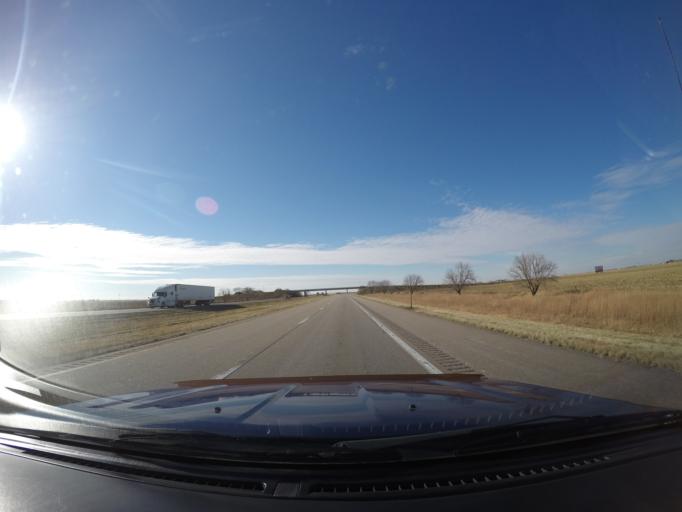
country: US
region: Nebraska
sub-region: York County
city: York
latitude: 40.8221
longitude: -97.7467
